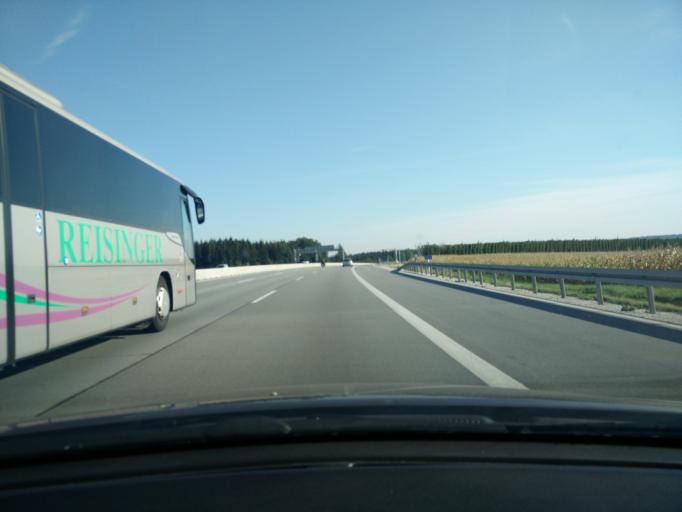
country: DE
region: Bavaria
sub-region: Upper Bavaria
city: Schweitenkirchen
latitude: 48.5216
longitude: 11.5836
